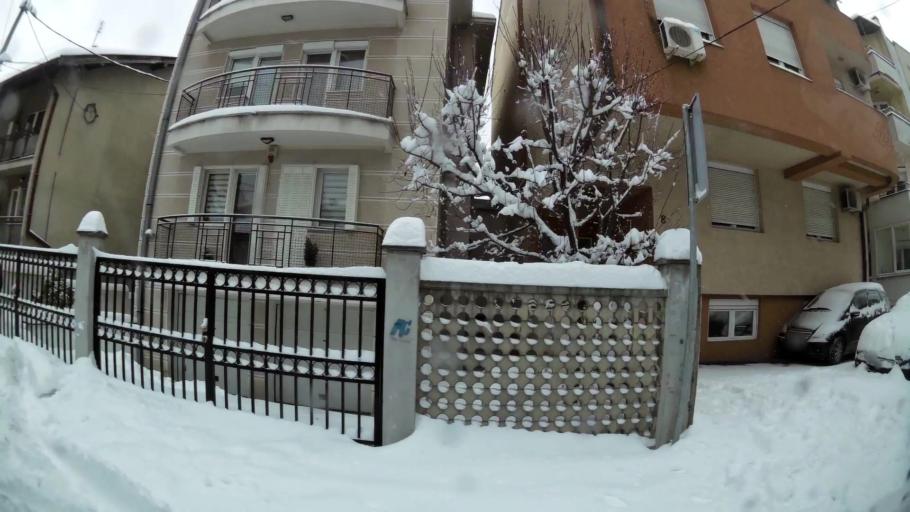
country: RS
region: Central Serbia
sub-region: Belgrade
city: Vracar
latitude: 44.7881
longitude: 20.4807
